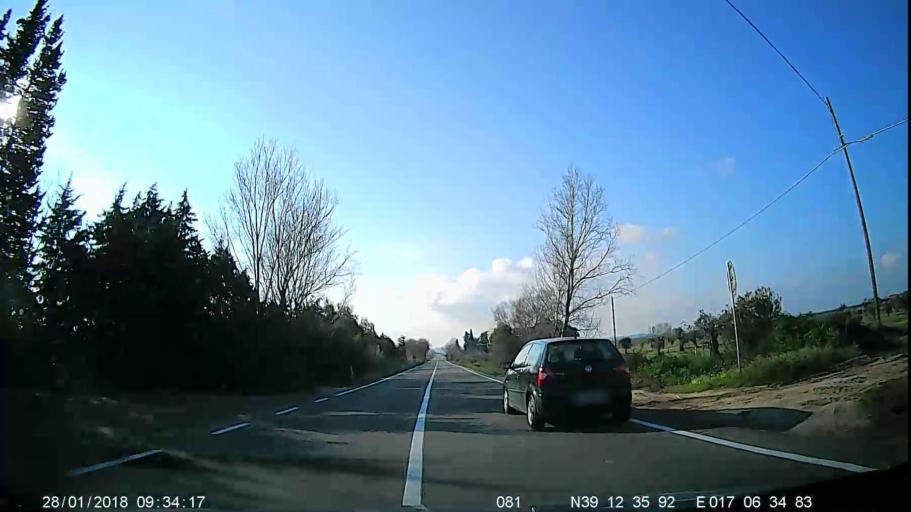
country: IT
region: Calabria
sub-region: Provincia di Crotone
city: Tronca
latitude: 39.2094
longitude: 17.1096
